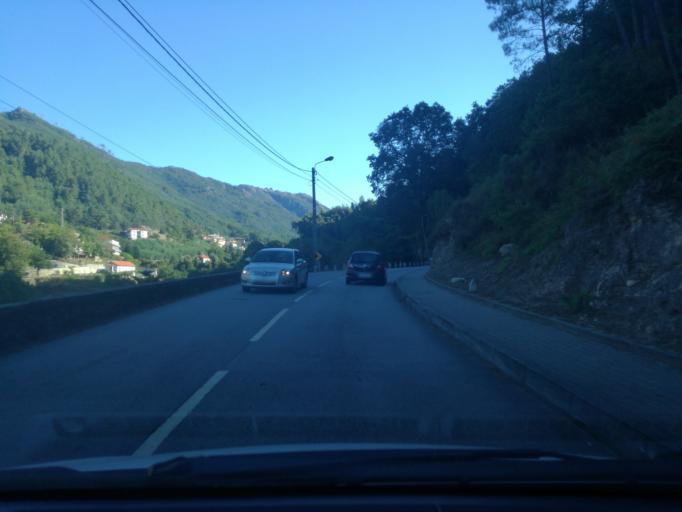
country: PT
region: Braga
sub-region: Vieira do Minho
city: Real
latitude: 41.7180
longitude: -8.1646
